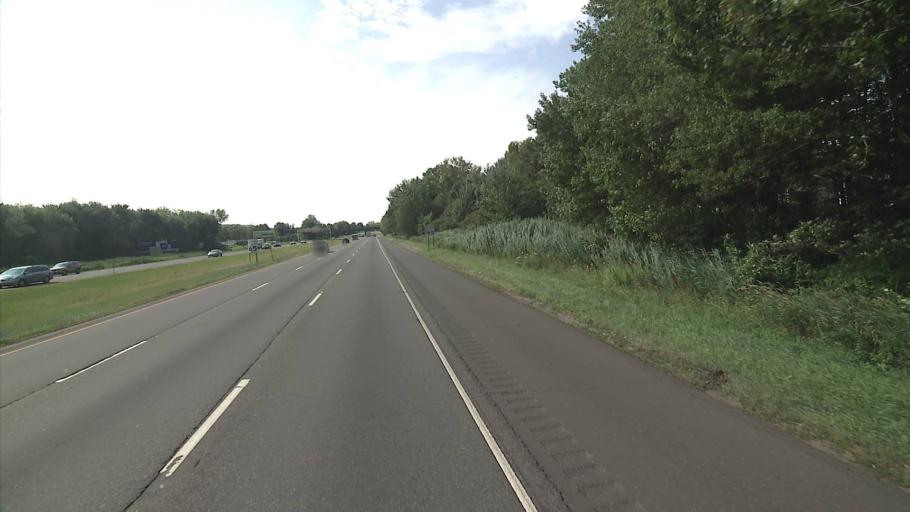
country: US
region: Connecticut
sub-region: New Haven County
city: Meriden
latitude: 41.5153
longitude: -72.7706
